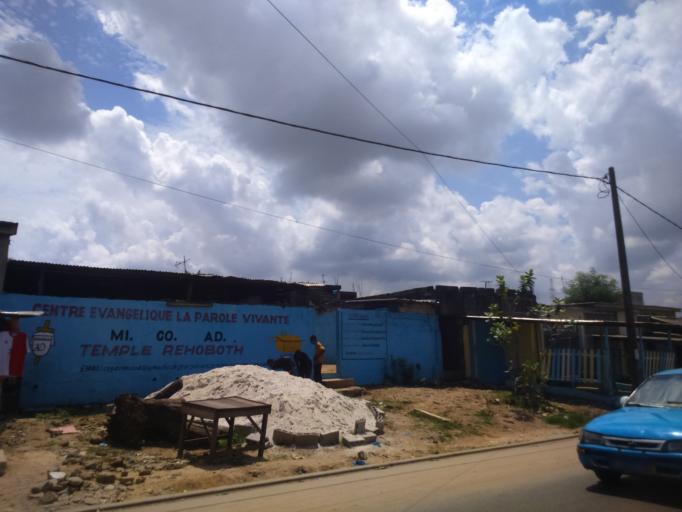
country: CI
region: Lagunes
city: Abidjan
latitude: 5.3396
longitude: -4.0900
